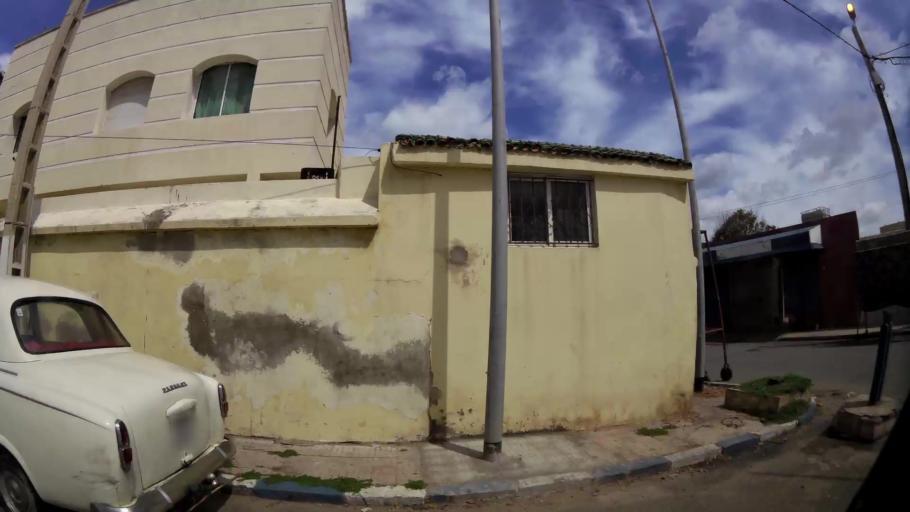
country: MA
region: Grand Casablanca
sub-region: Casablanca
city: Casablanca
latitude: 33.6182
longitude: -7.5414
